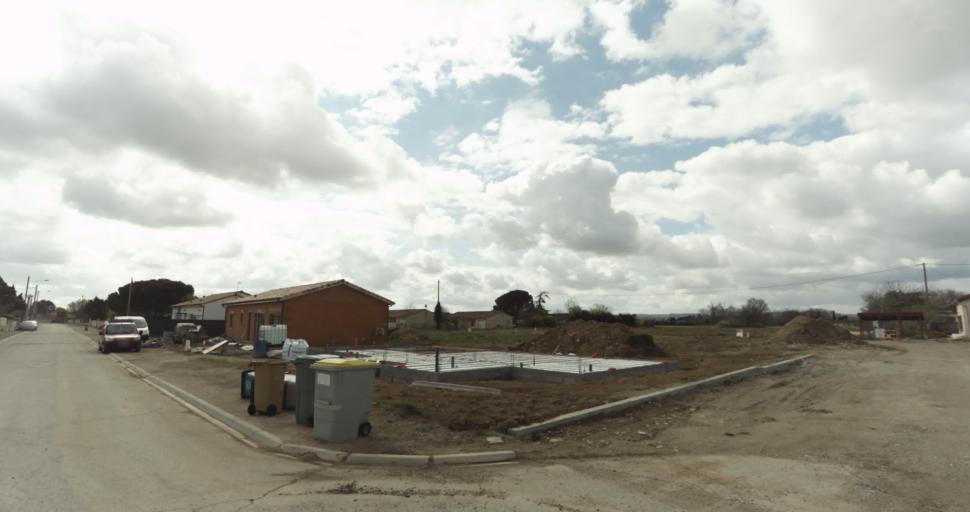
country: FR
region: Midi-Pyrenees
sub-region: Departement de la Haute-Garonne
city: Auterive
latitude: 43.3743
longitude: 1.4548
